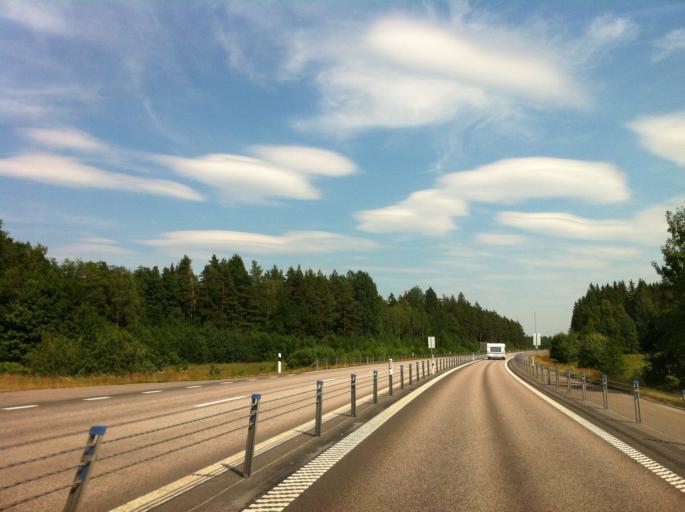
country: SE
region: Kalmar
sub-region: Nybro Kommun
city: Nybro
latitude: 56.7268
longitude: 15.9952
